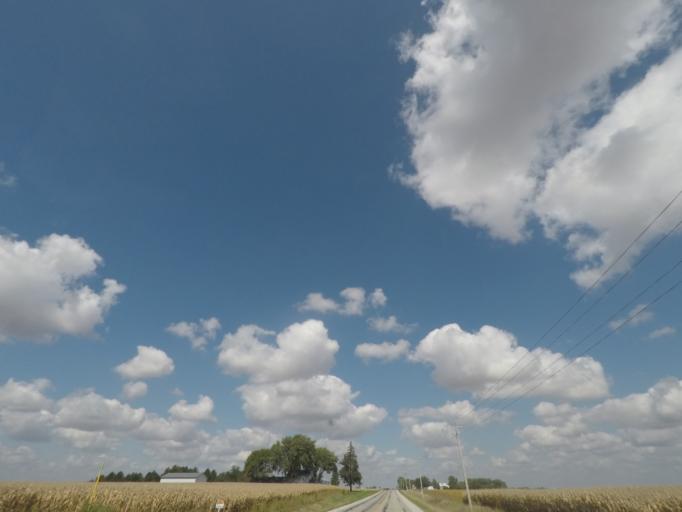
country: US
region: Iowa
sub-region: Story County
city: Nevada
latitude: 42.0384
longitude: -93.4058
